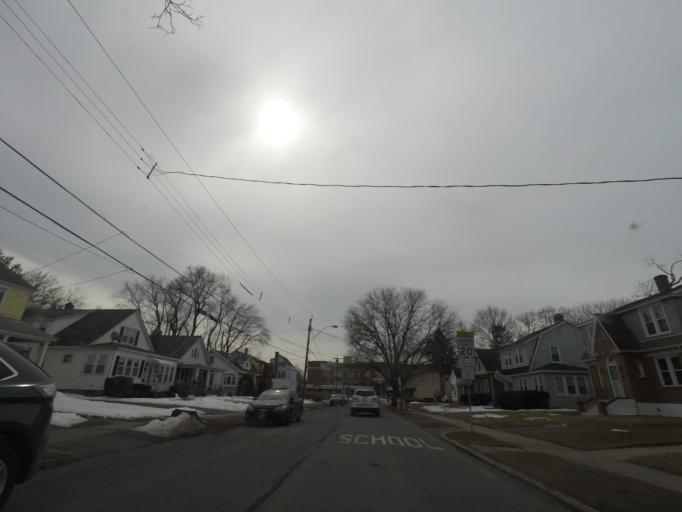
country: US
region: New York
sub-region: Albany County
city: Albany
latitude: 42.6430
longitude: -73.7884
